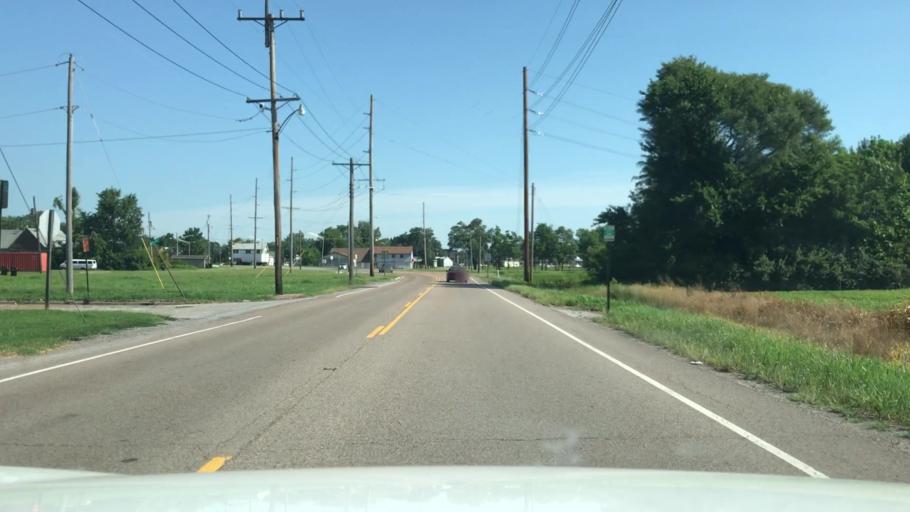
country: US
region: Illinois
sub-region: Madison County
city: Venice
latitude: 38.6675
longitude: -90.1703
